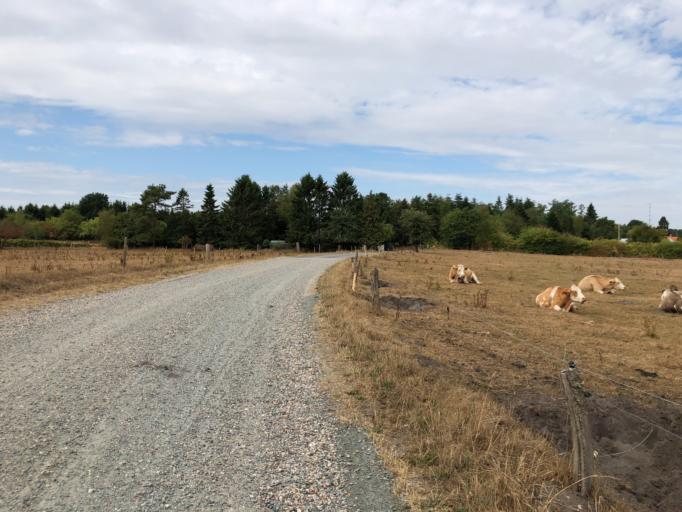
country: DK
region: South Denmark
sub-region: Vejle Kommune
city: Egtved
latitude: 55.6549
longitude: 9.2636
